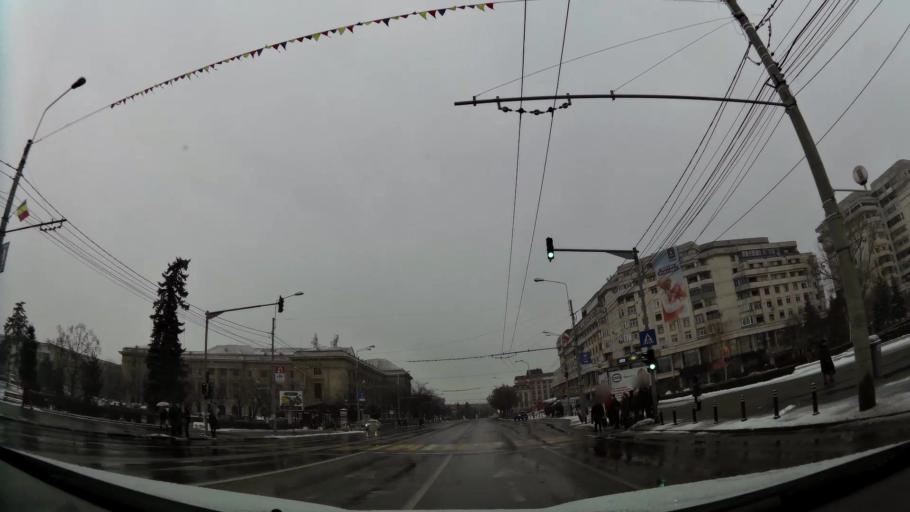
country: RO
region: Prahova
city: Ploiesti
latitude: 44.9423
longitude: 26.0200
